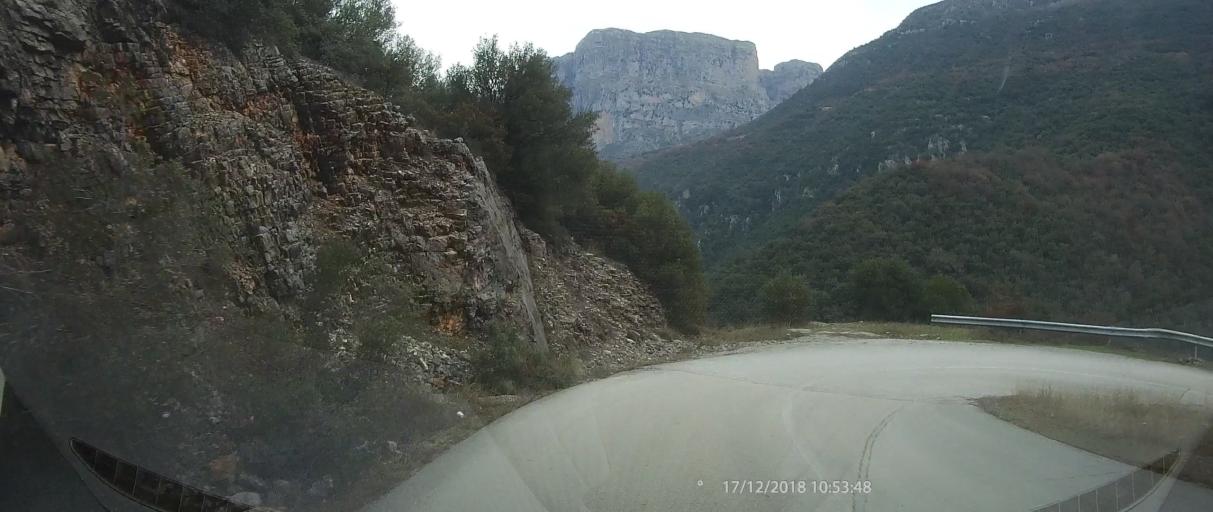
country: GR
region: Epirus
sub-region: Nomos Ioanninon
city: Kalpaki
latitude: 39.9477
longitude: 20.6888
